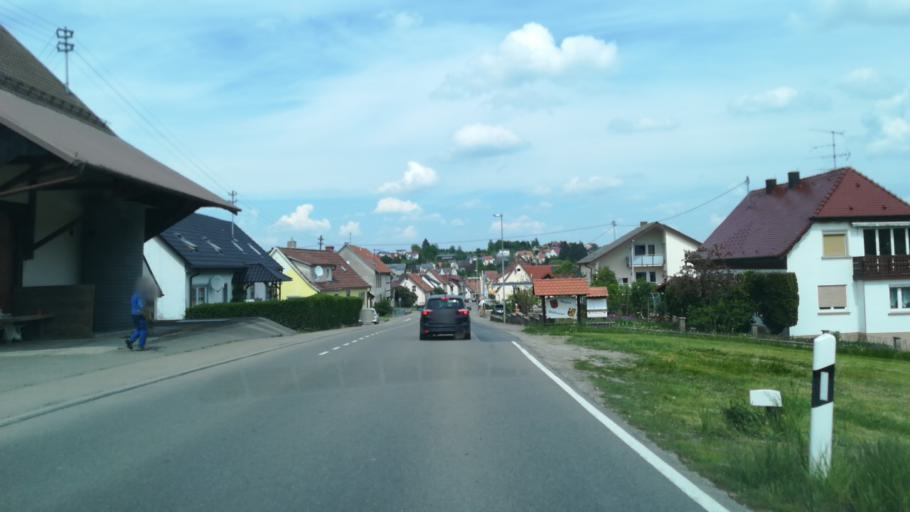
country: DE
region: Baden-Wuerttemberg
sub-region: Freiburg Region
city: Muhlingen
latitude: 47.8937
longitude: 9.0368
